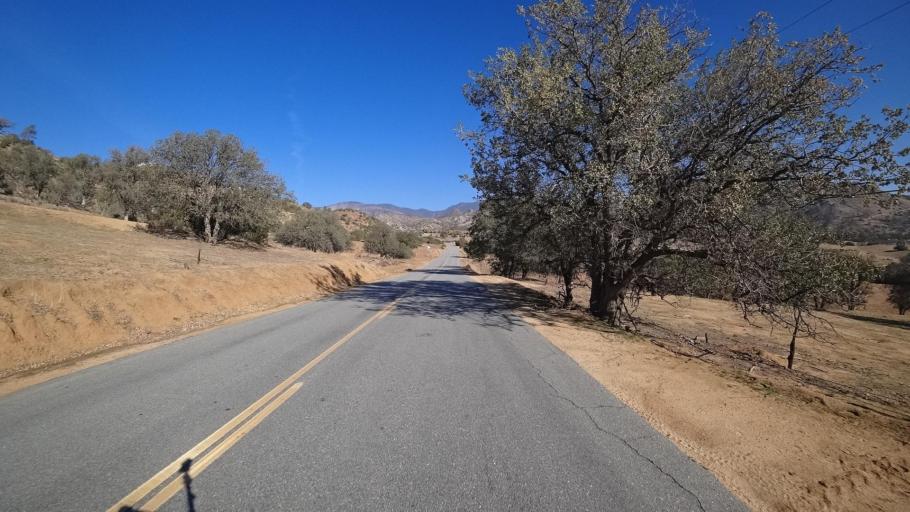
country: US
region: California
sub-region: Kern County
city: Tehachapi
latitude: 35.3511
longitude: -118.3840
